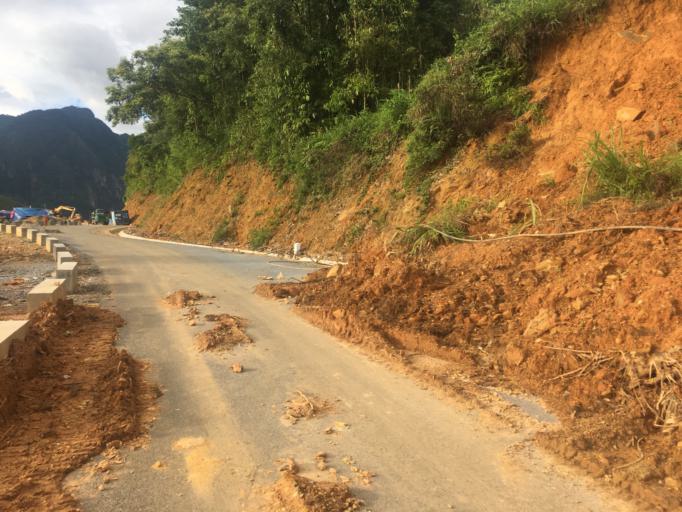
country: VN
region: Ha Giang
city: Thi Tran Tam Son
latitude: 22.9498
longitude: 105.0256
